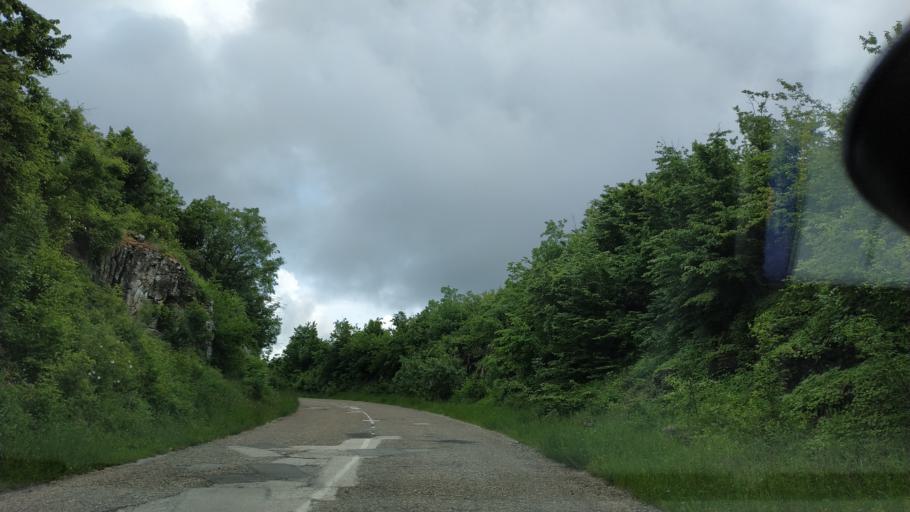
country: RS
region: Central Serbia
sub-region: Zajecarski Okrug
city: Boljevac
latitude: 43.7224
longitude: 21.9501
